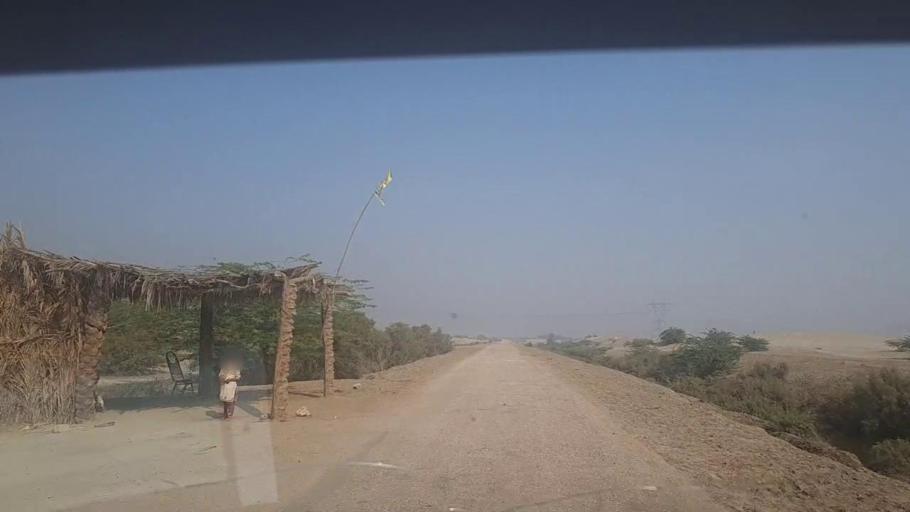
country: PK
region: Sindh
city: Khairpur
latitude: 27.4445
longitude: 68.7170
